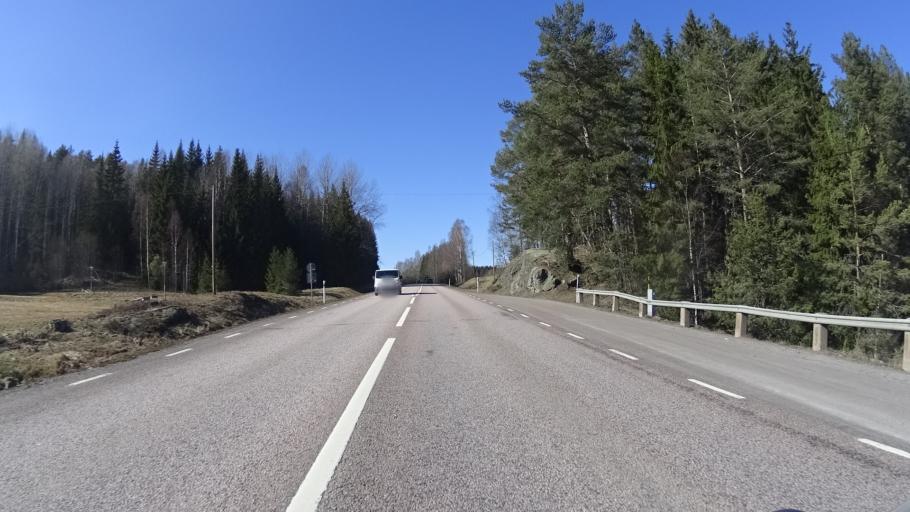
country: SE
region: Vaermland
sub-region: Karlstads Kommun
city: Edsvalla
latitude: 59.5342
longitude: 13.1102
